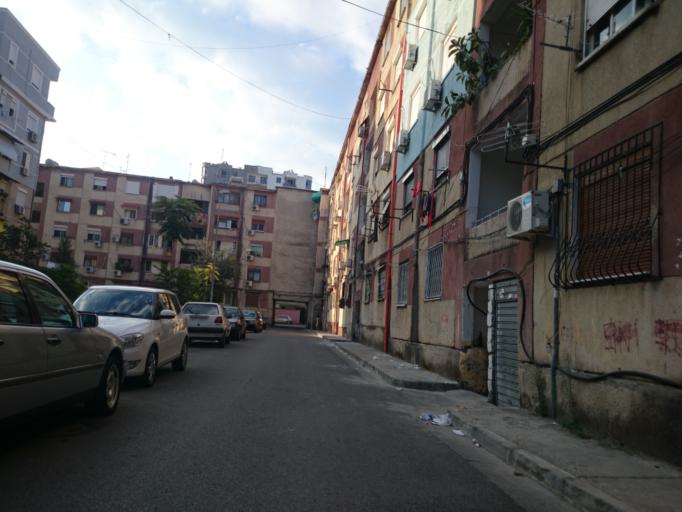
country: AL
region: Tirane
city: Tirana
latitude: 41.3254
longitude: 19.7947
